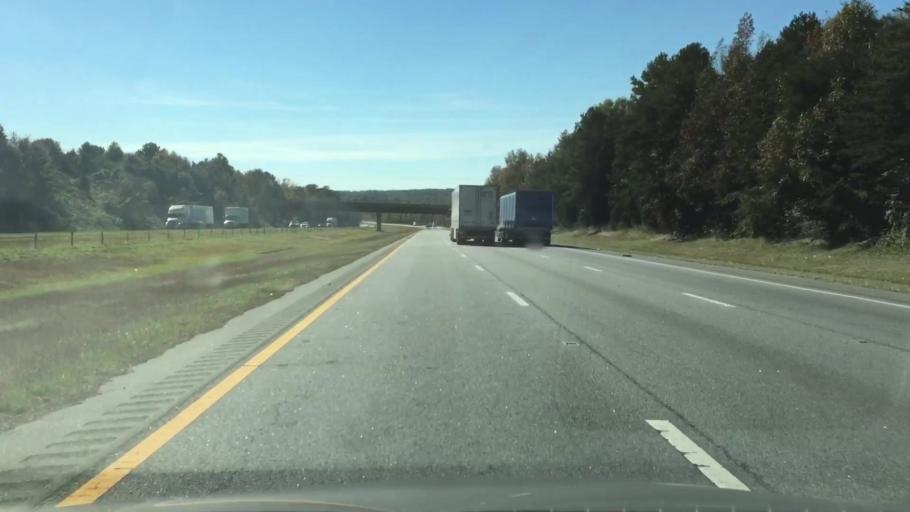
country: US
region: North Carolina
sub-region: Randolph County
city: Trinity
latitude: 35.8889
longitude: -79.9870
